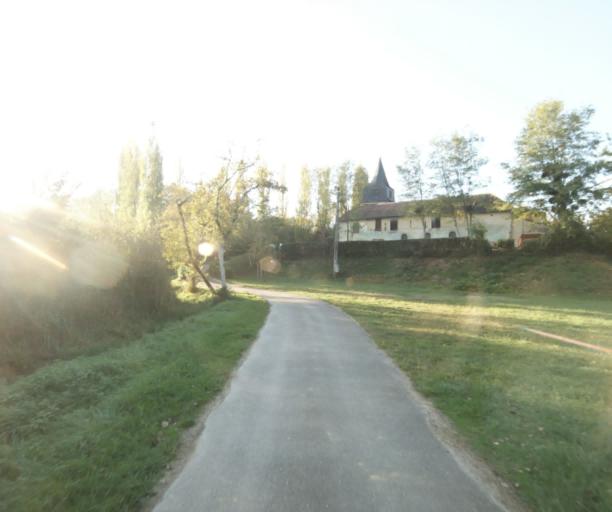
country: FR
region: Midi-Pyrenees
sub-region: Departement du Gers
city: Eauze
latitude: 43.7615
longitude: 0.1624
